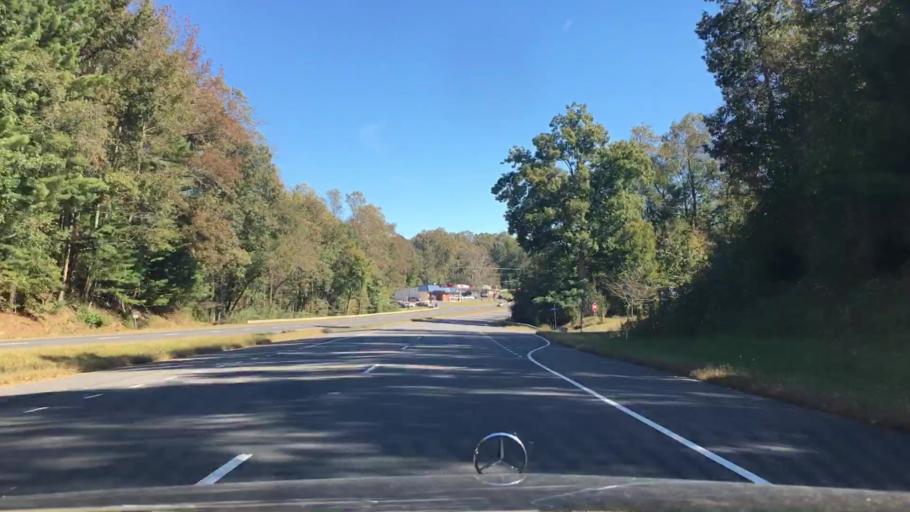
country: US
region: Virginia
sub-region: King George County
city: King George
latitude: 38.2795
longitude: -77.2255
